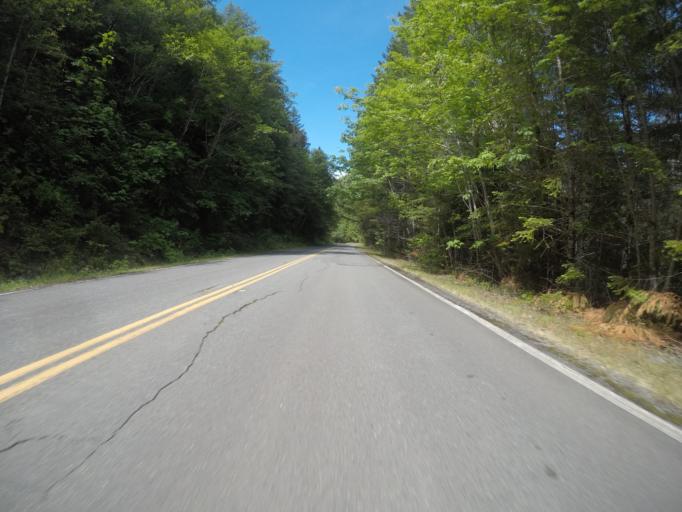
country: US
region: California
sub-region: Del Norte County
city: Bertsch-Oceanview
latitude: 41.7257
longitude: -123.9652
